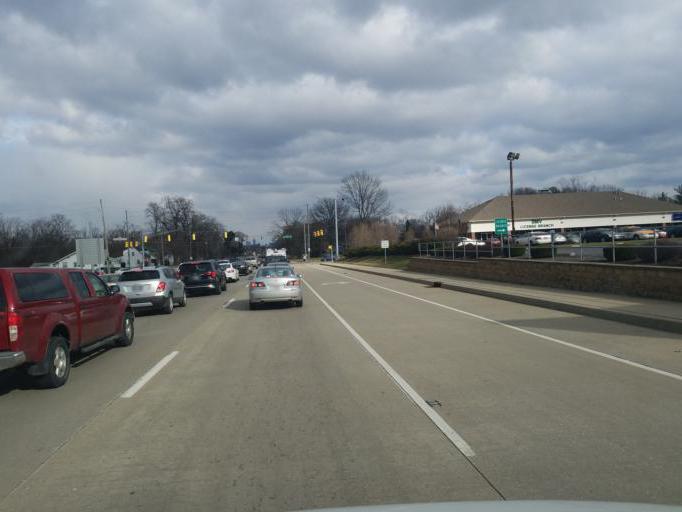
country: US
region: Indiana
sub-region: Marion County
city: Speedway
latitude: 39.7649
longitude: -86.2615
